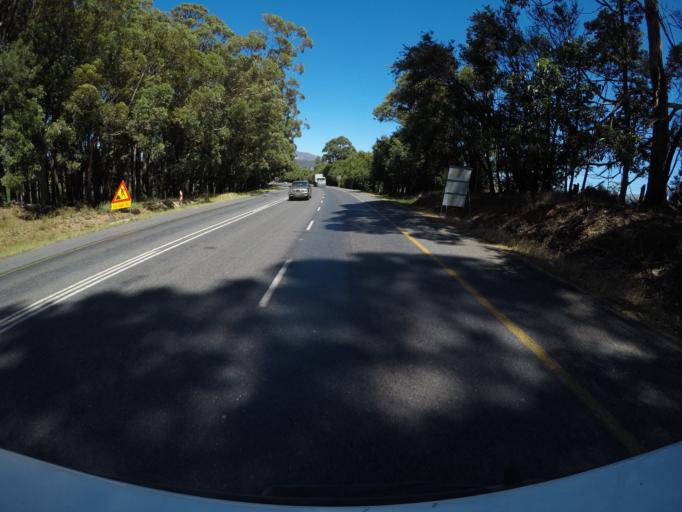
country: ZA
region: Western Cape
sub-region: Overberg District Municipality
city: Grabouw
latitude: -34.1626
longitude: 19.0300
